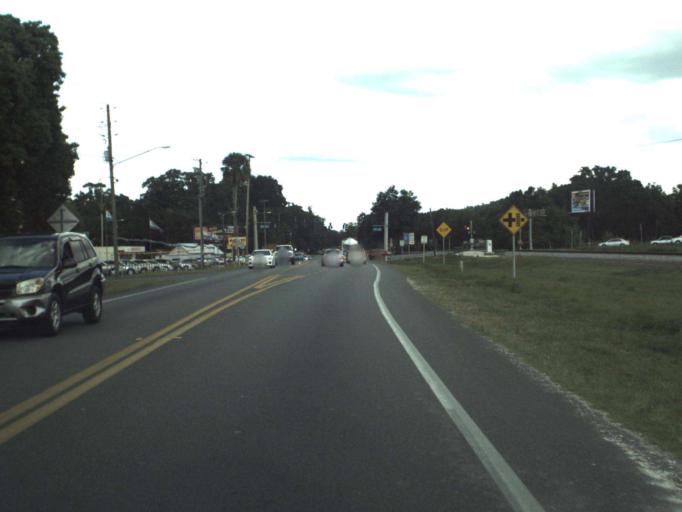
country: US
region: Florida
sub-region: Marion County
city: Belleview
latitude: 29.0632
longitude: -82.0495
